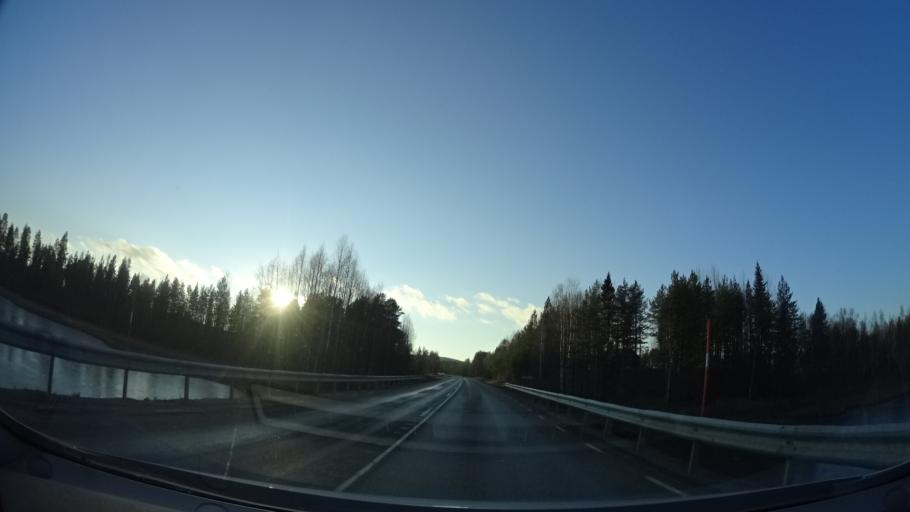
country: SE
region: Vaesterbotten
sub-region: Lycksele Kommun
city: Lycksele
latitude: 64.8150
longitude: 18.7523
